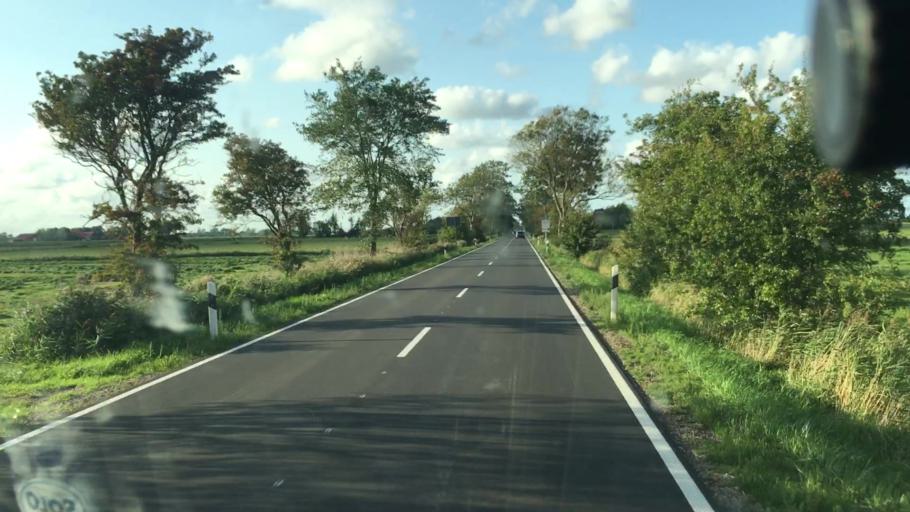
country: DE
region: Lower Saxony
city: Jever
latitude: 53.6166
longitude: 7.8662
